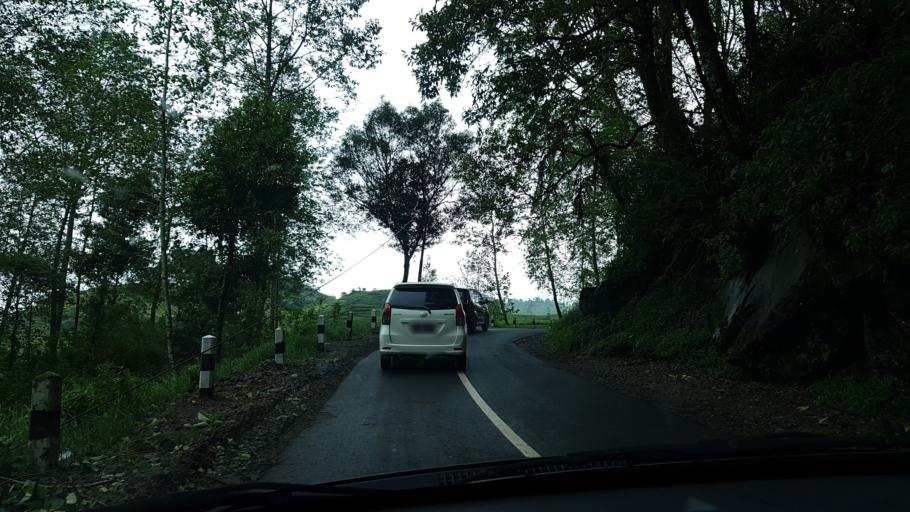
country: ID
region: West Java
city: Banjar
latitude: -7.1507
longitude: 107.3826
